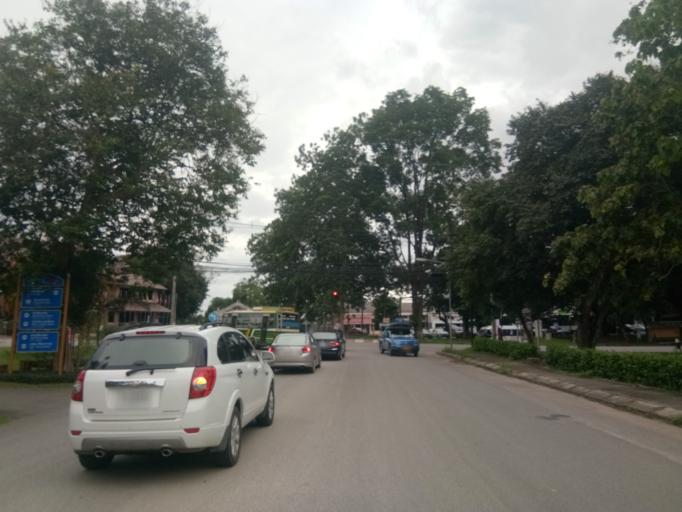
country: TH
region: Chiang Rai
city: Chiang Rai
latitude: 19.9827
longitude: 99.8512
